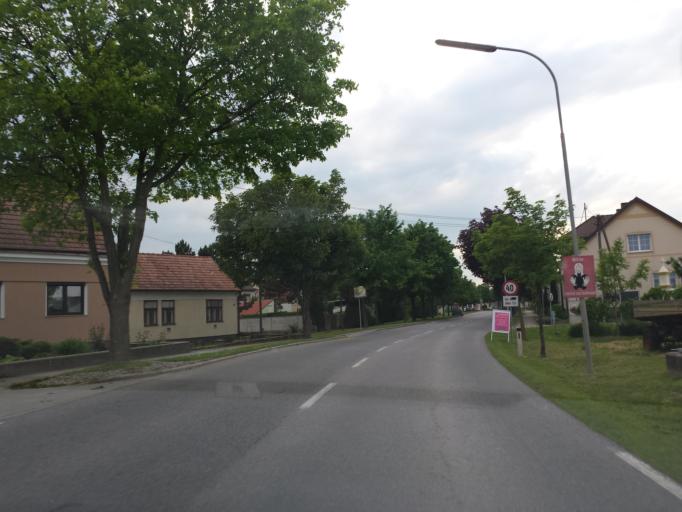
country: AT
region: Lower Austria
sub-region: Politischer Bezirk Ganserndorf
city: Markgrafneusiedl
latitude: 48.2633
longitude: 16.6375
